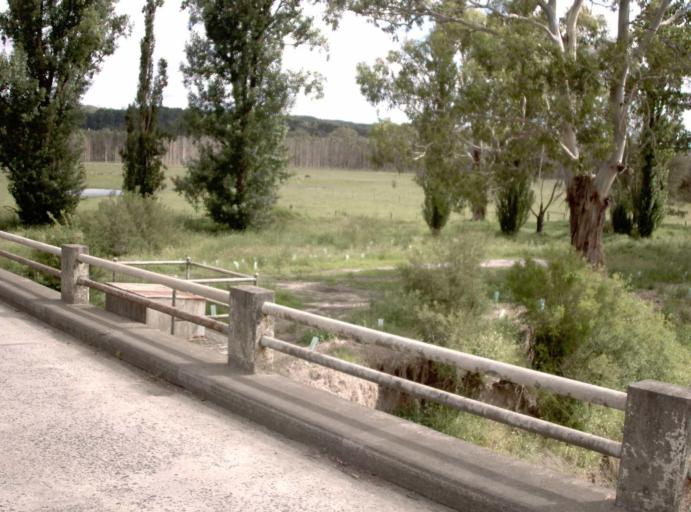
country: AU
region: Victoria
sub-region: Latrobe
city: Morwell
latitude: -38.1673
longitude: 146.4110
